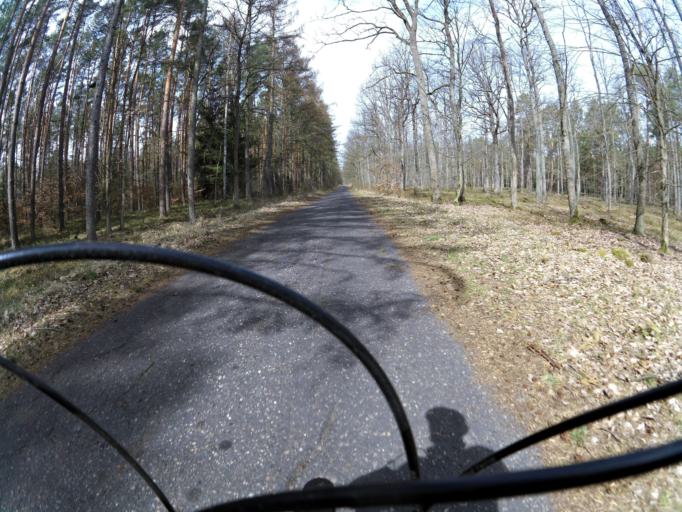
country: PL
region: West Pomeranian Voivodeship
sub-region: Powiat mysliborski
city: Boleszkowice
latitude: 52.6982
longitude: 14.5158
